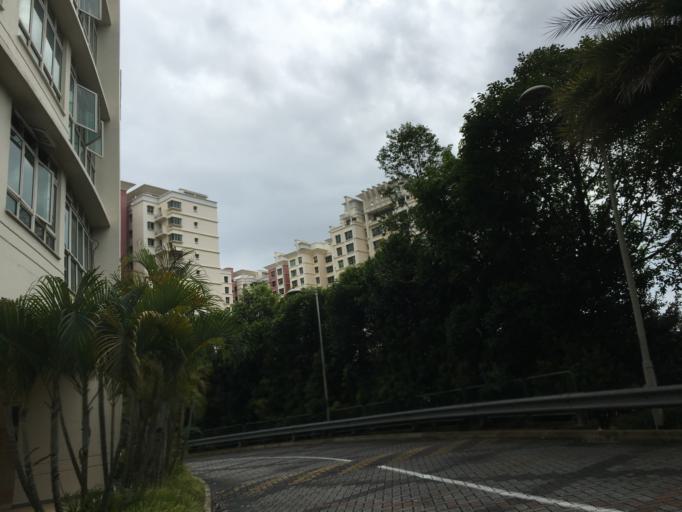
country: MY
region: Johor
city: Kampung Pasir Gudang Baru
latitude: 1.3812
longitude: 103.8967
